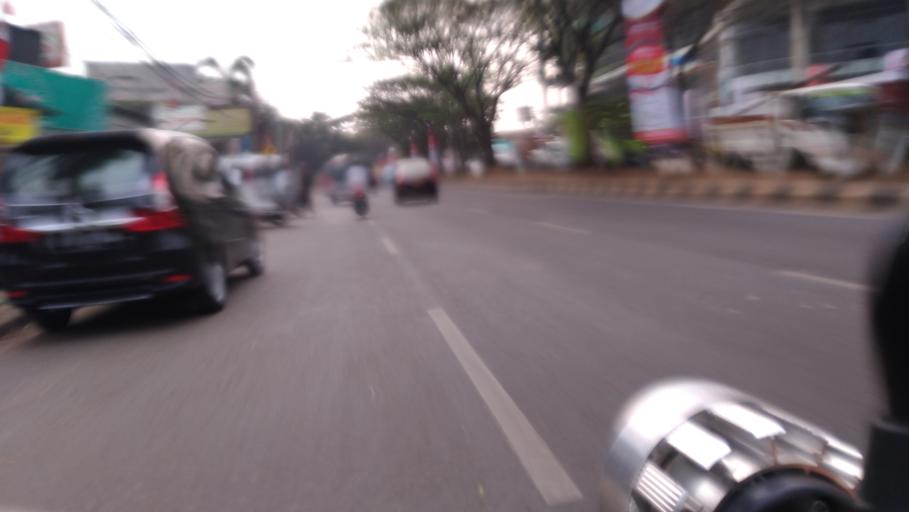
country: ID
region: West Java
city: Cileungsir
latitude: -6.3760
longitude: 106.9028
